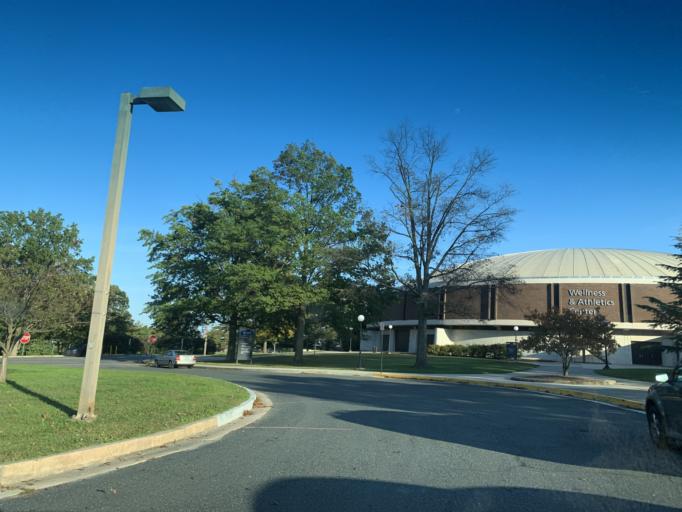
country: US
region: Maryland
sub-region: Baltimore County
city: Rossville
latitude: 39.3550
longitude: -76.4793
